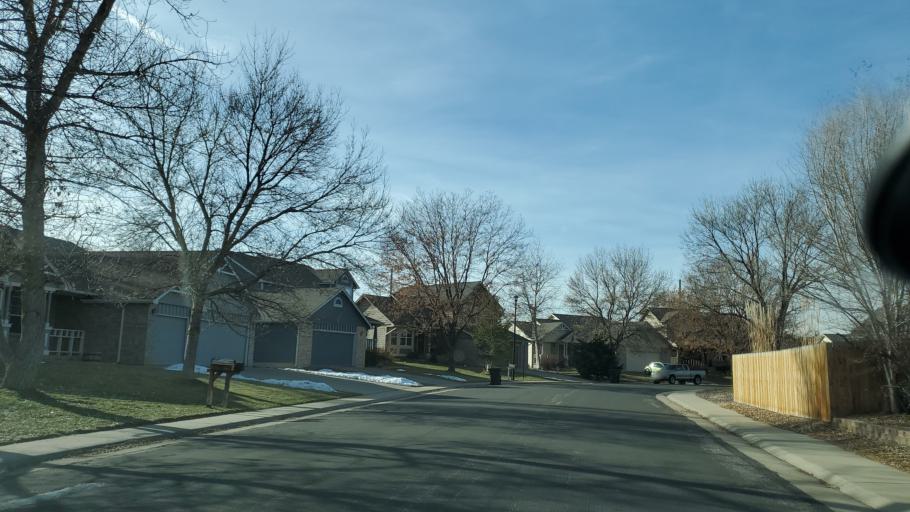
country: US
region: Colorado
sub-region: Adams County
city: Northglenn
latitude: 39.9155
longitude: -104.9567
